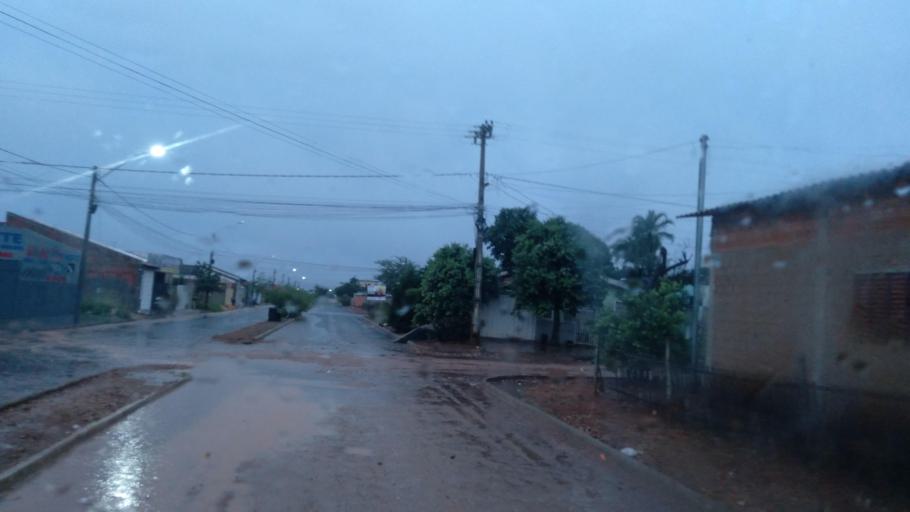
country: BR
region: Goias
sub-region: Mineiros
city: Mineiros
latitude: -17.5415
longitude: -52.5465
